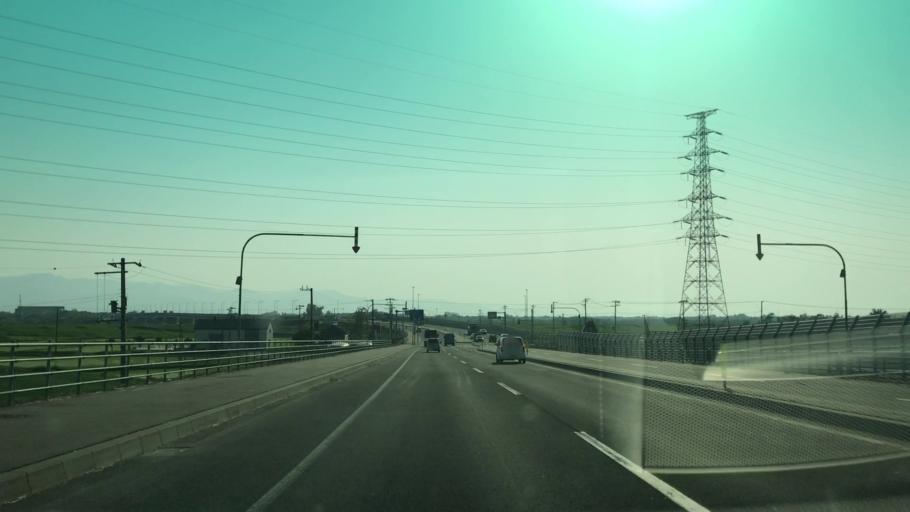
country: JP
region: Hokkaido
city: Tobetsu
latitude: 43.1767
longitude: 141.4314
